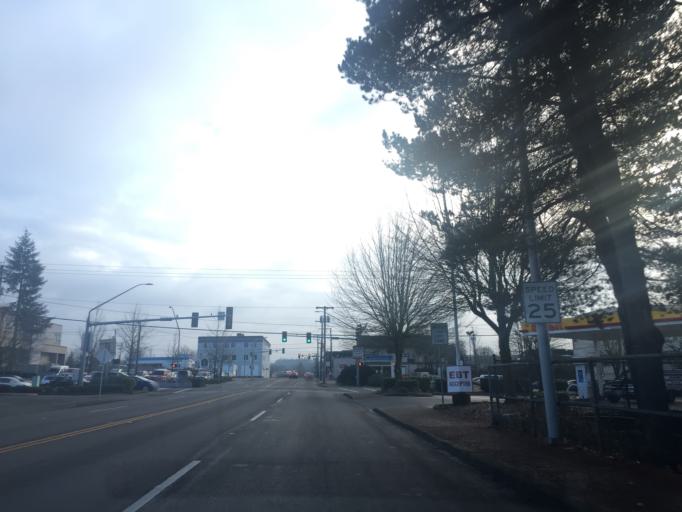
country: US
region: Washington
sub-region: Thurston County
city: Olympia
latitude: 47.0471
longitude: -122.8931
